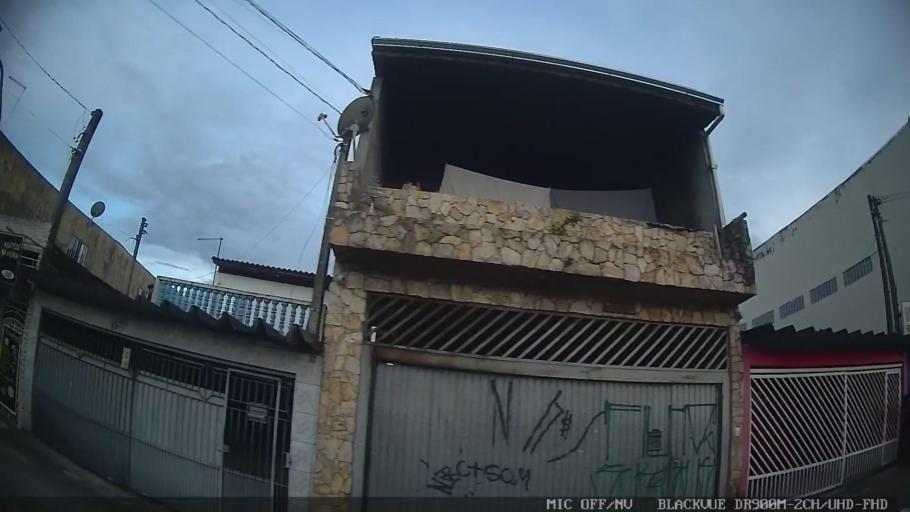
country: BR
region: Sao Paulo
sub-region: Itaquaquecetuba
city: Itaquaquecetuba
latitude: -23.4986
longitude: -46.3162
